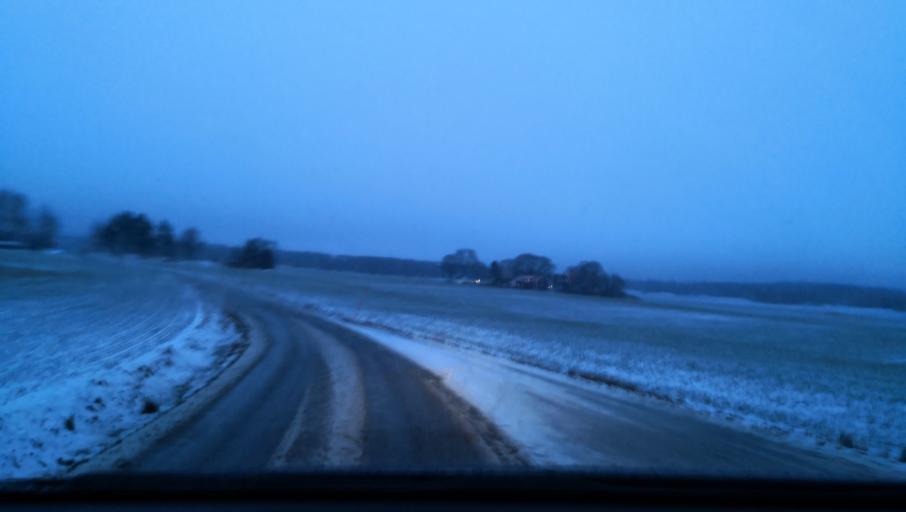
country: SE
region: Soedermanland
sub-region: Eskilstuna Kommun
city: Kvicksund
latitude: 59.3741
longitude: 16.2993
